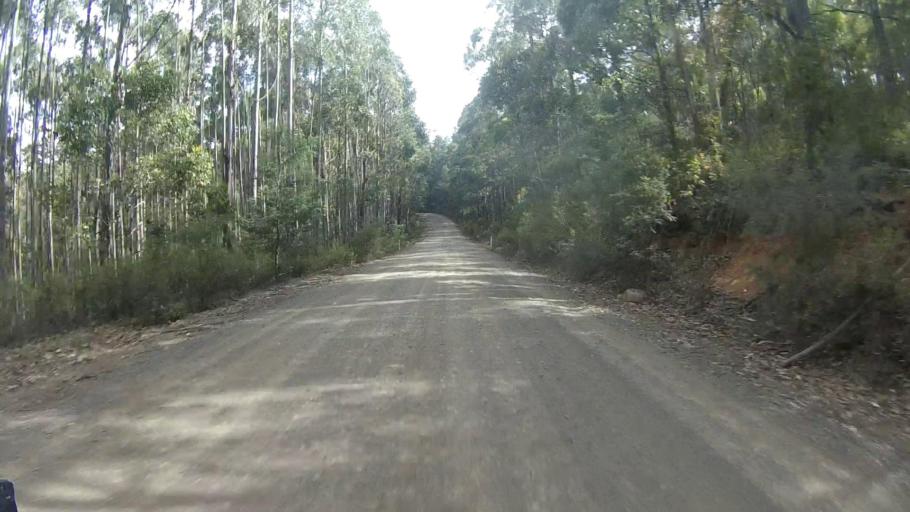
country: AU
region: Tasmania
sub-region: Sorell
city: Sorell
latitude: -42.7486
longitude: 147.8288
